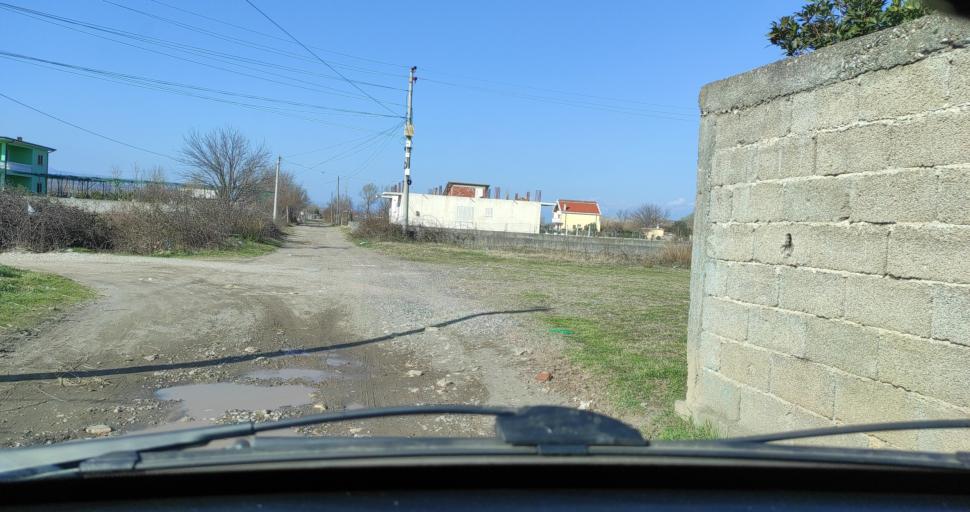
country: AL
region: Shkoder
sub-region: Rrethi i Shkodres
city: Velipoje
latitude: 41.8697
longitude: 19.4114
